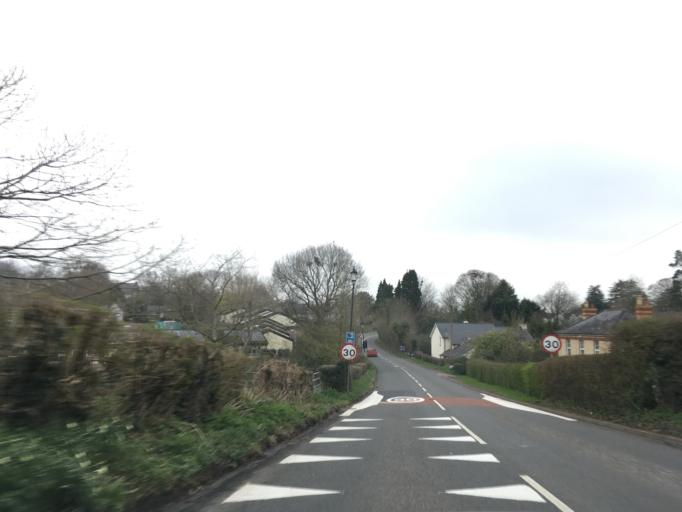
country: GB
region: Wales
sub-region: Monmouthshire
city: Llangybi
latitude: 51.6633
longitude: -2.9076
